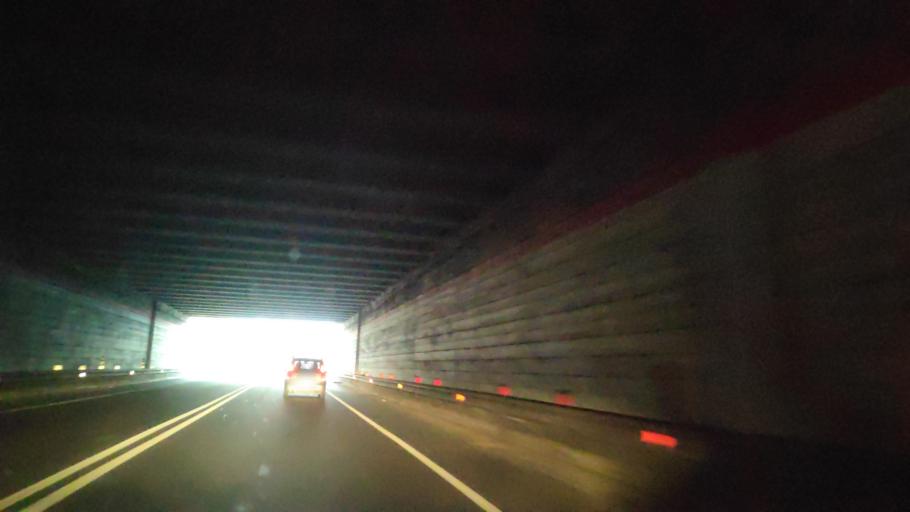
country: IT
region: Calabria
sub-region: Provincia di Catanzaro
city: Soverato Superiore
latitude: 38.6946
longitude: 16.5388
